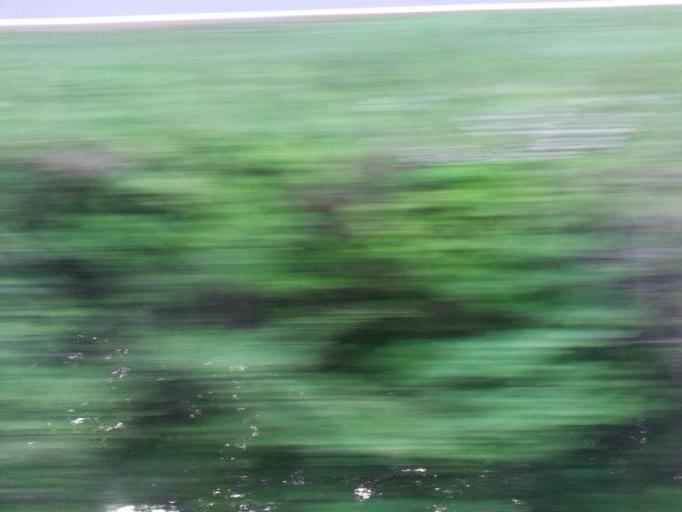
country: US
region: Tennessee
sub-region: McMinn County
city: Etowah
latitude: 35.2244
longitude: -84.3317
